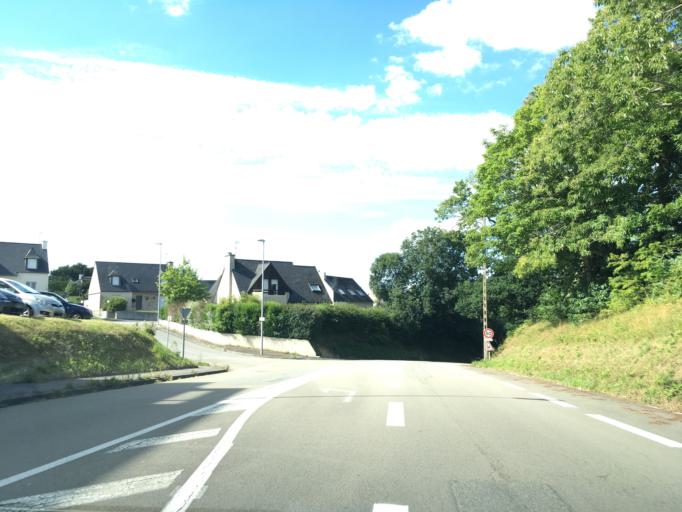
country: FR
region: Brittany
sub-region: Departement du Finistere
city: Quimper
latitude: 47.9853
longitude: -4.0756
